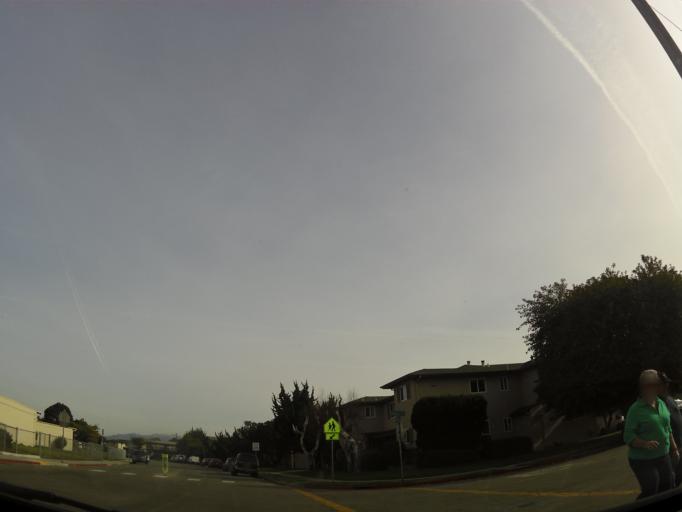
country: US
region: California
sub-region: Monterey County
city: Salinas
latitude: 36.6701
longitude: -121.6793
